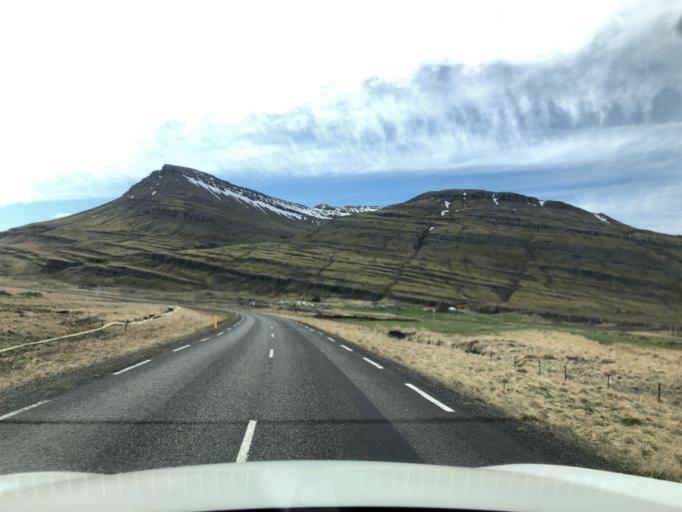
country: IS
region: East
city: Eskifjoerdur
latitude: 64.7691
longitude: -14.0540
